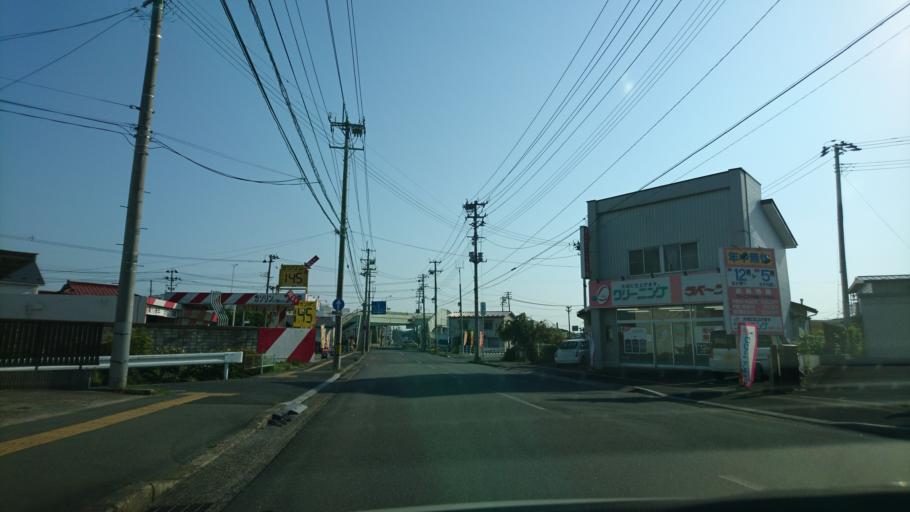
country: JP
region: Iwate
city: Ichinoseki
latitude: 38.9319
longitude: 141.1233
